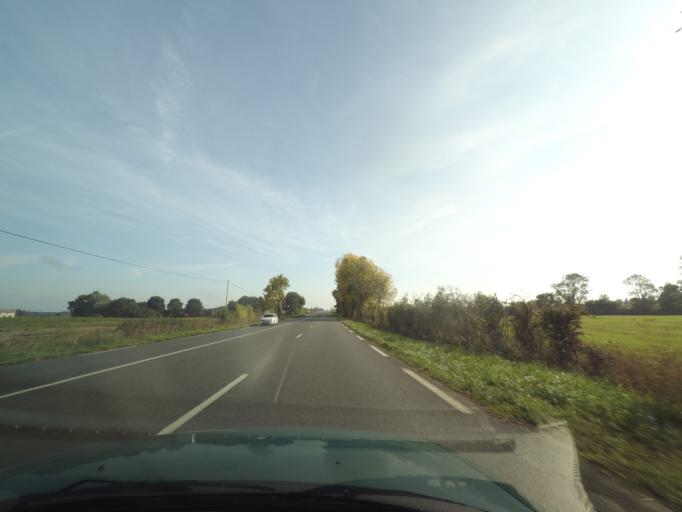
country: FR
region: Pays de la Loire
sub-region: Departement de Maine-et-Loire
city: Vihiers
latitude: 47.1506
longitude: -0.4683
